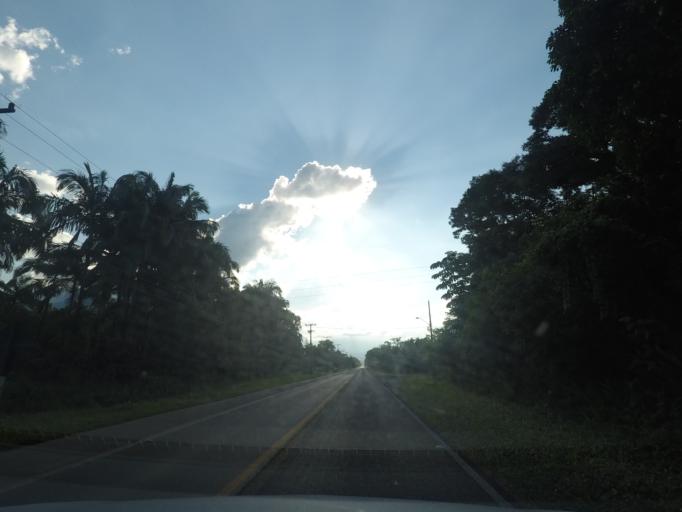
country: BR
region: Parana
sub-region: Antonina
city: Antonina
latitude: -25.4698
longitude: -48.8432
